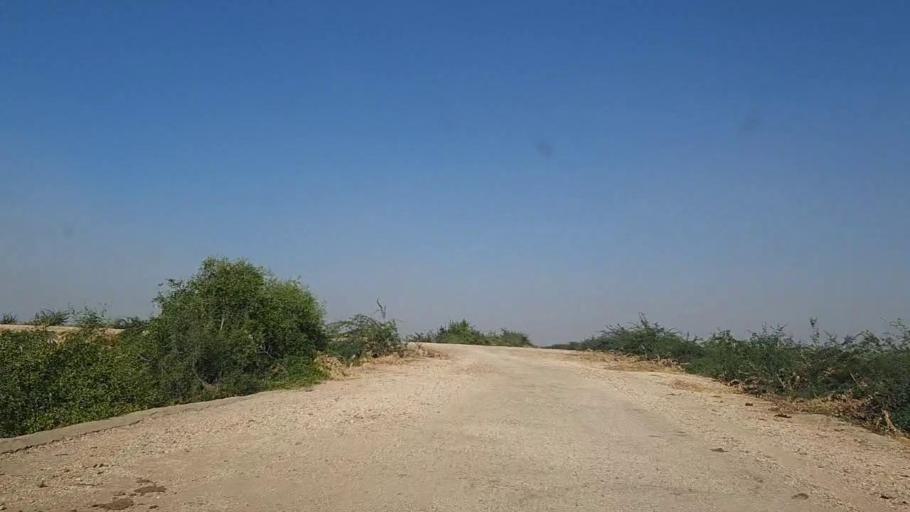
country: PK
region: Sindh
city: Daro Mehar
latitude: 25.0039
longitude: 68.1213
